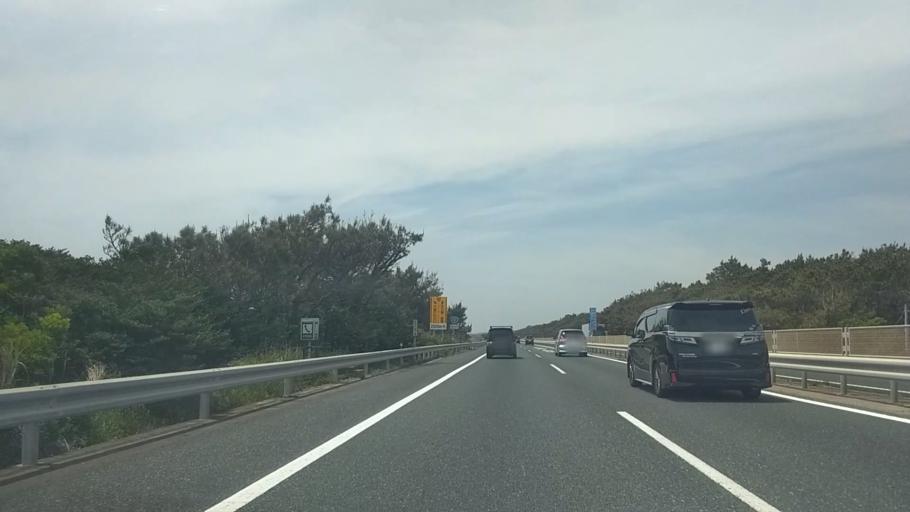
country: JP
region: Shizuoka
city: Kosai-shi
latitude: 34.6805
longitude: 137.5591
